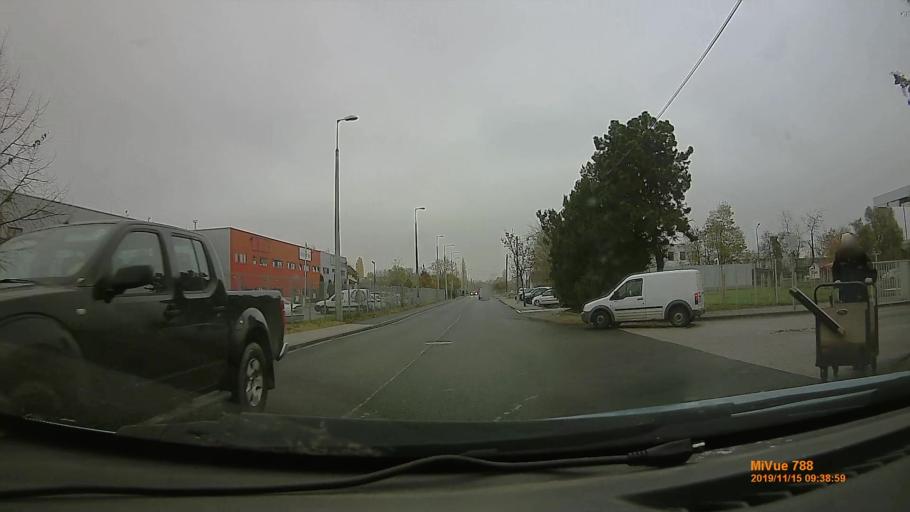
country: HU
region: Budapest
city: Budapest XX. keruelet
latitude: 47.4568
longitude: 19.1035
